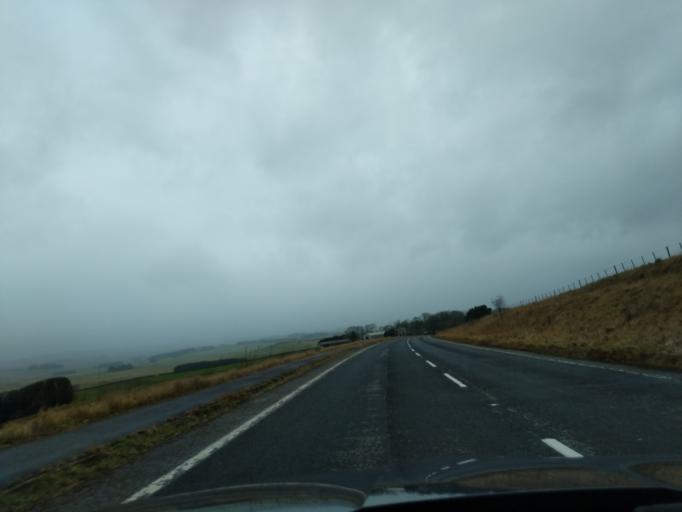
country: GB
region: England
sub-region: Northumberland
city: Otterburn
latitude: 55.2181
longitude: -2.1307
